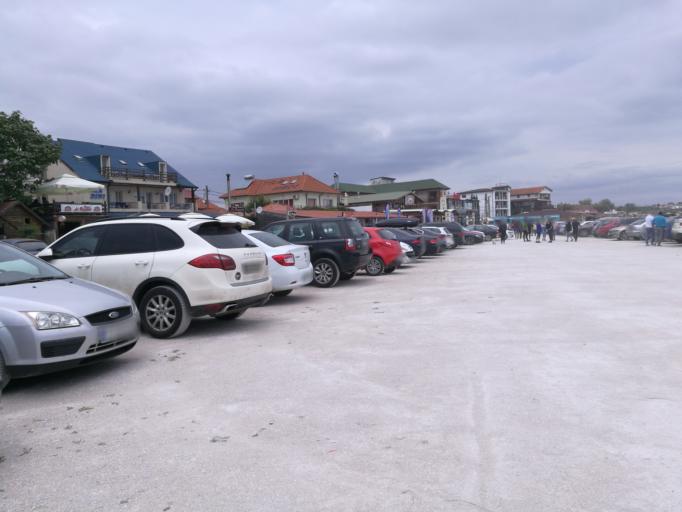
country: RO
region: Constanta
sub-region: Municipiul Mangalia
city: Mangalia
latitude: 43.7525
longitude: 28.5750
